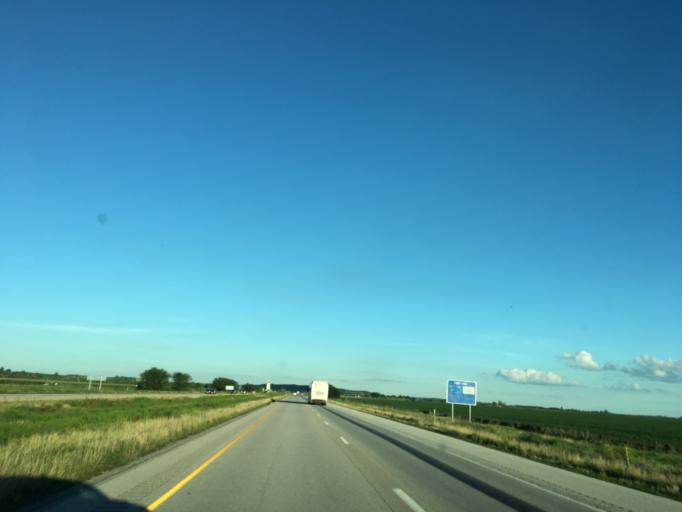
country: US
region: Iowa
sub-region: Fremont County
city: Hamburg
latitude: 40.6131
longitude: -95.6922
